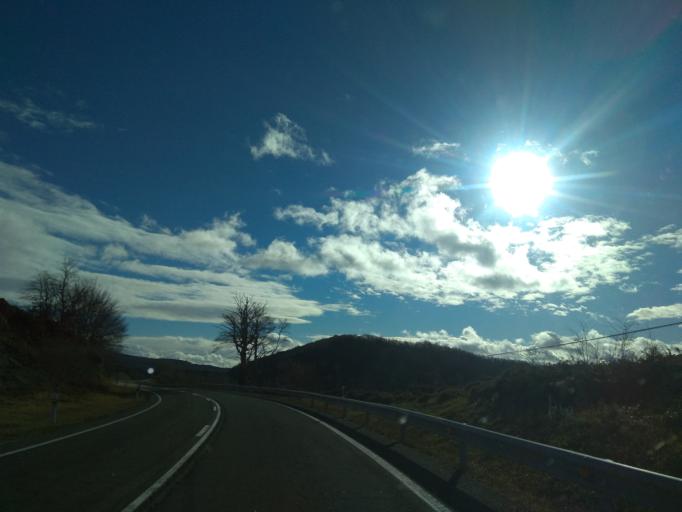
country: ES
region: Cantabria
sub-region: Provincia de Cantabria
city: San Martin de Elines
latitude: 42.9347
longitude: -3.8294
